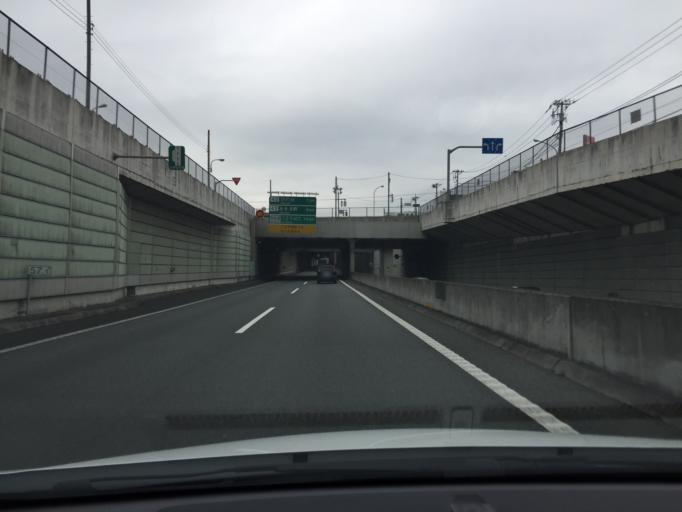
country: JP
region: Saitama
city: Hanno
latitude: 35.7939
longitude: 139.3098
